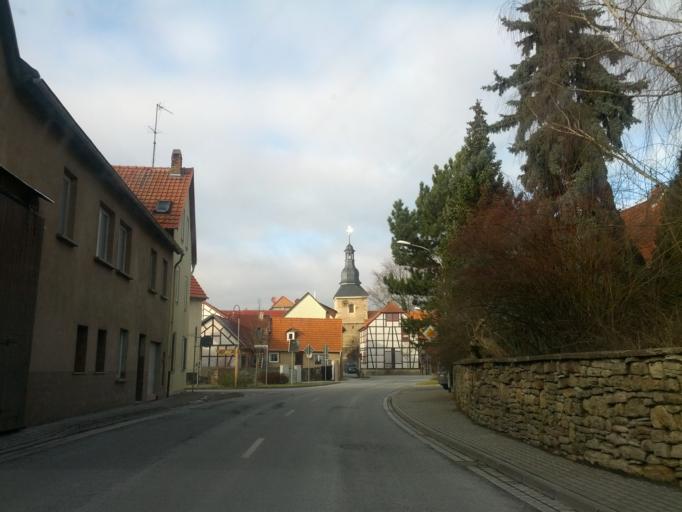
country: DE
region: Thuringia
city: Bad Langensalza
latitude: 51.0983
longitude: 10.6278
